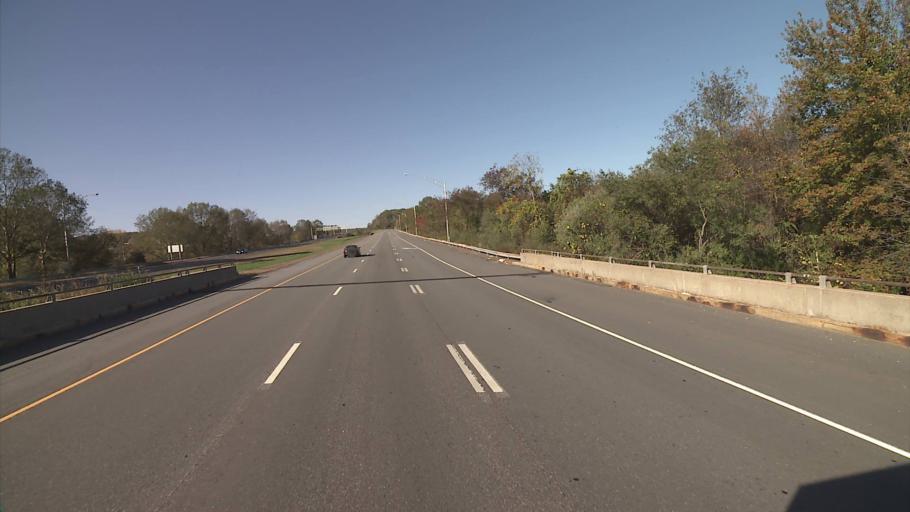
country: US
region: Connecticut
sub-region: Tolland County
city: Mansfield City
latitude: 41.7240
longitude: -72.2520
